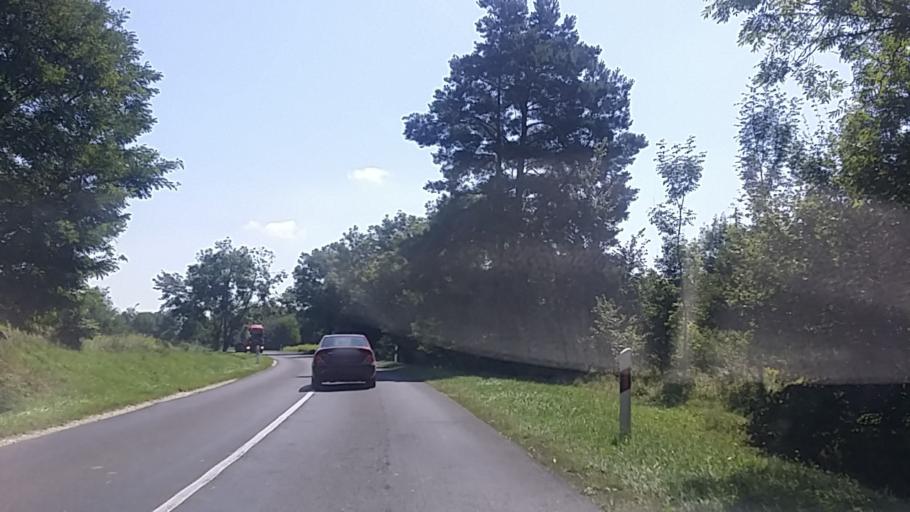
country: HU
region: Zala
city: Keszthely
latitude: 46.7034
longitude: 17.2404
